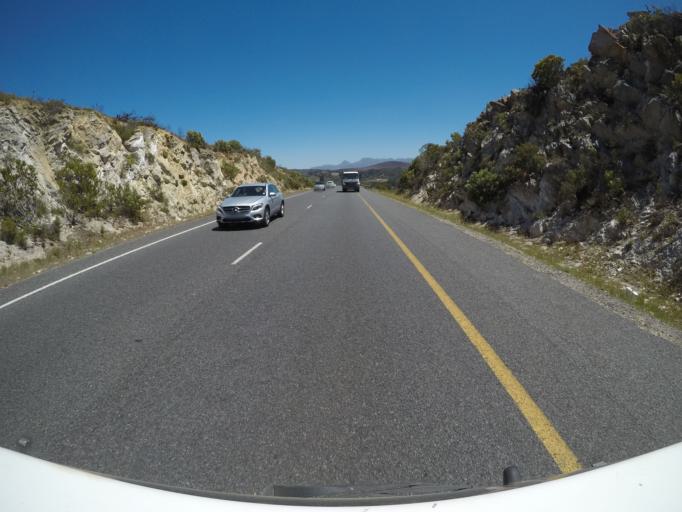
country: ZA
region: Western Cape
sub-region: Overberg District Municipality
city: Grabouw
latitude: -34.2146
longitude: 19.1698
